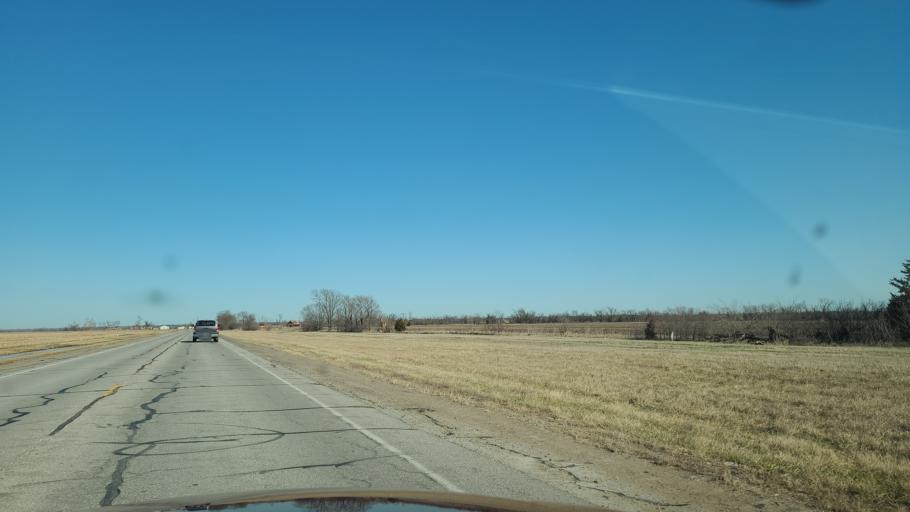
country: US
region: Kansas
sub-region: Douglas County
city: Lawrence
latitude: 38.9427
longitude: -95.1741
